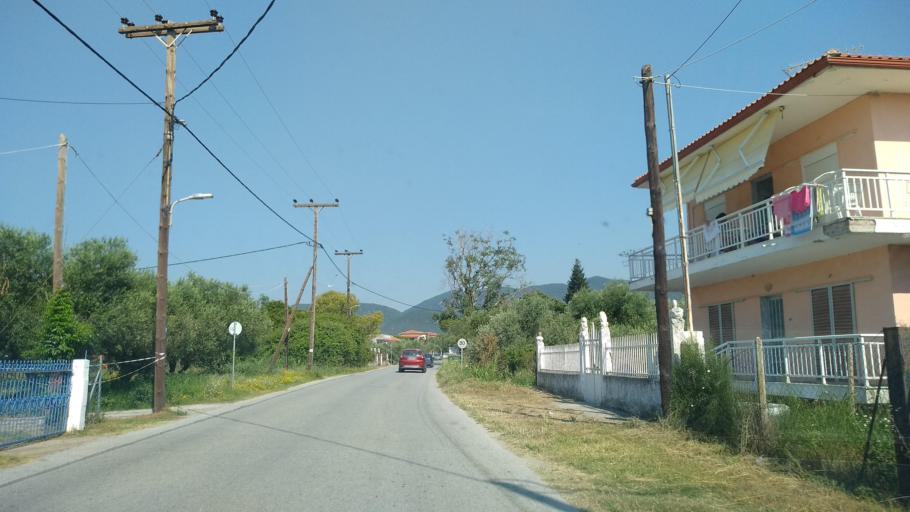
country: GR
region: Central Macedonia
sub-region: Nomos Thessalonikis
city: Nea Vrasna
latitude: 40.6900
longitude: 23.6873
